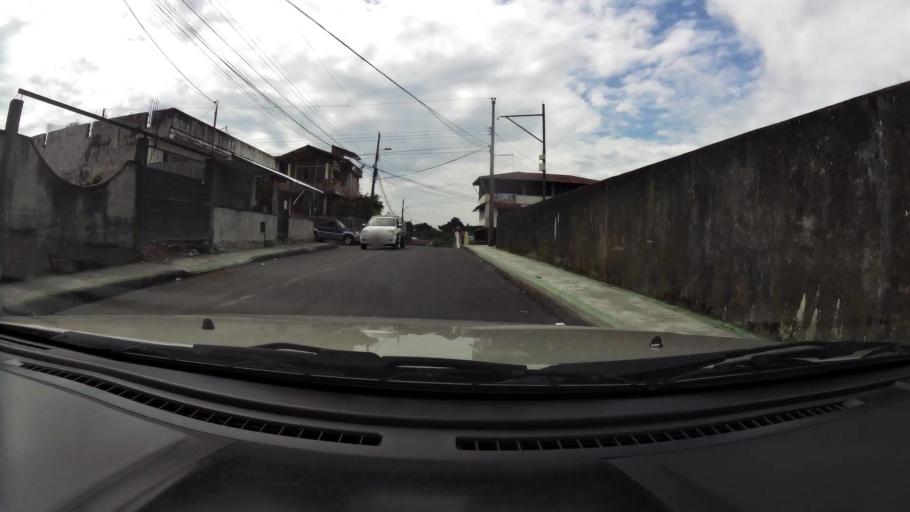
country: EC
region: Pastaza
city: Puyo
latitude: -1.4936
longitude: -77.9957
